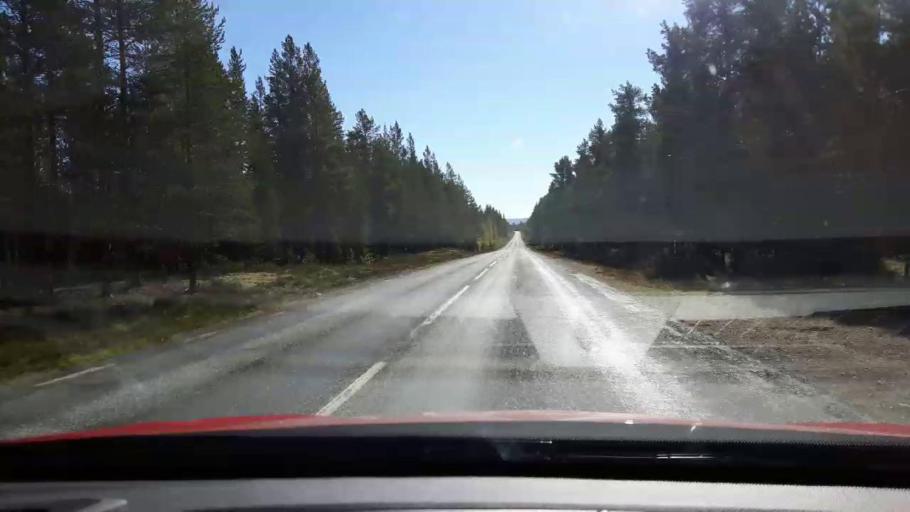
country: SE
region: Jaemtland
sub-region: Harjedalens Kommun
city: Sveg
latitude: 62.3743
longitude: 13.9784
